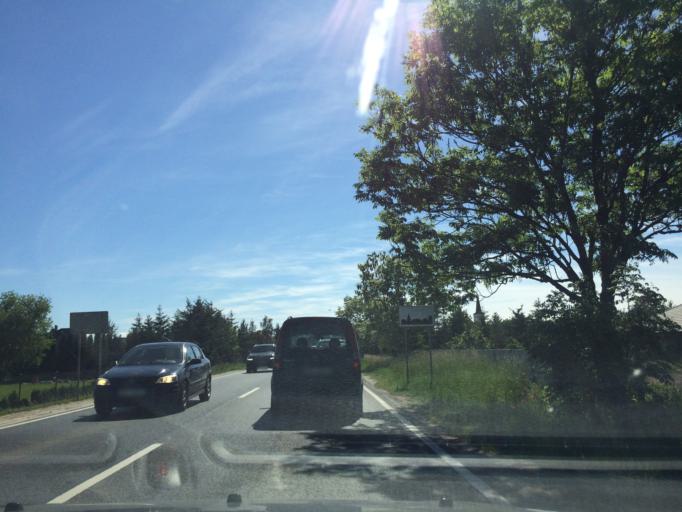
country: PL
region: Lower Silesian Voivodeship
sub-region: Powiat wroclawski
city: Gniechowice
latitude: 50.9899
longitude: 16.8385
